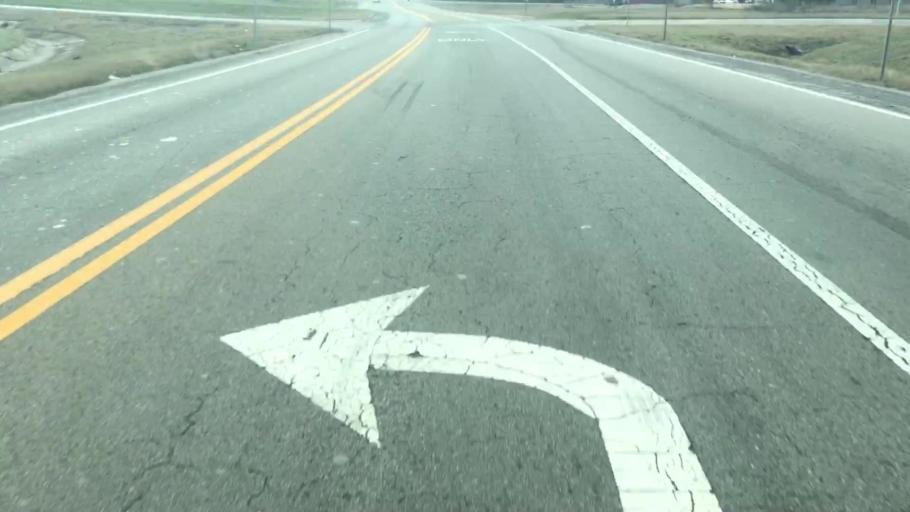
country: US
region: Alabama
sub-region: Walker County
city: Jasper
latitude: 33.7931
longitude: -87.2397
